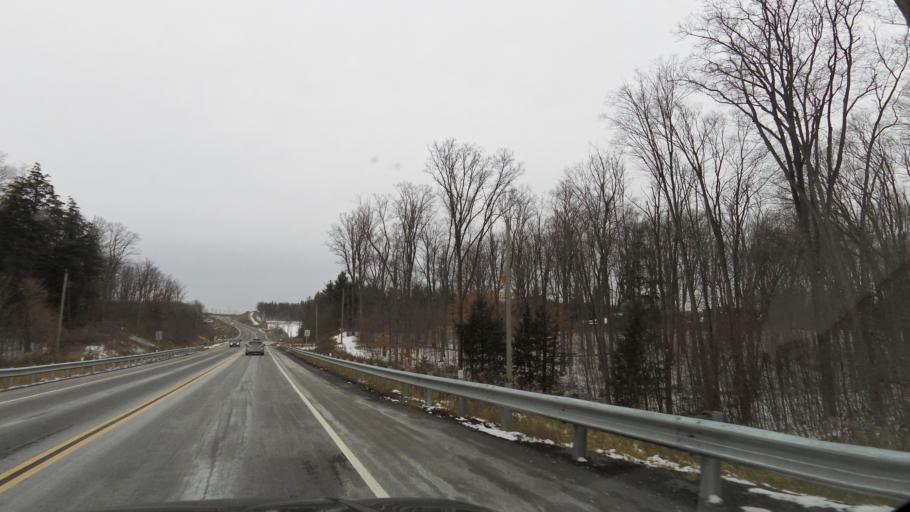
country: CA
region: Ontario
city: Newmarket
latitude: 44.0703
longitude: -79.5115
